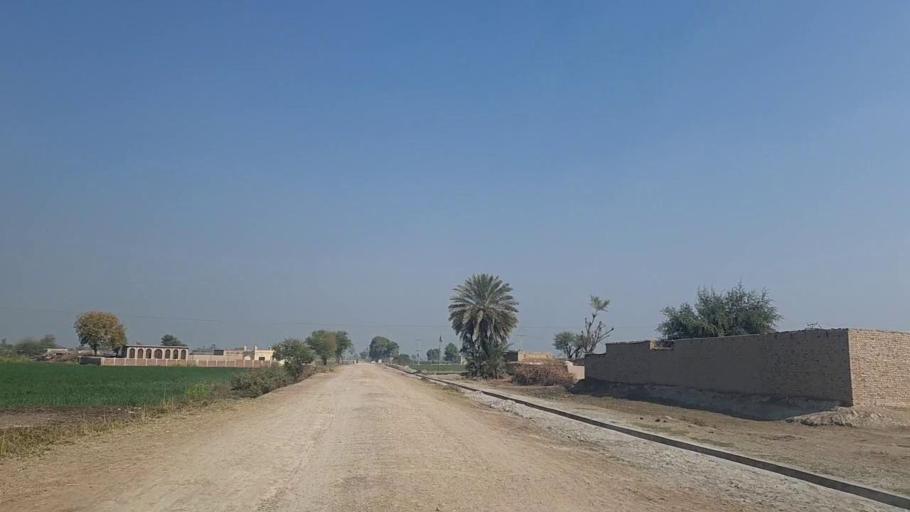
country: PK
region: Sindh
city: Nawabshah
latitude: 26.2279
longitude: 68.4905
